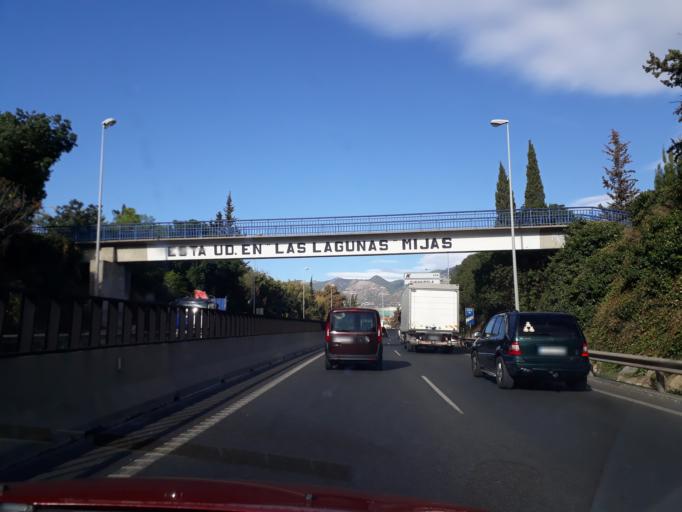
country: ES
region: Andalusia
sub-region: Provincia de Malaga
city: Fuengirola
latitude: 36.5429
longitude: -4.6346
